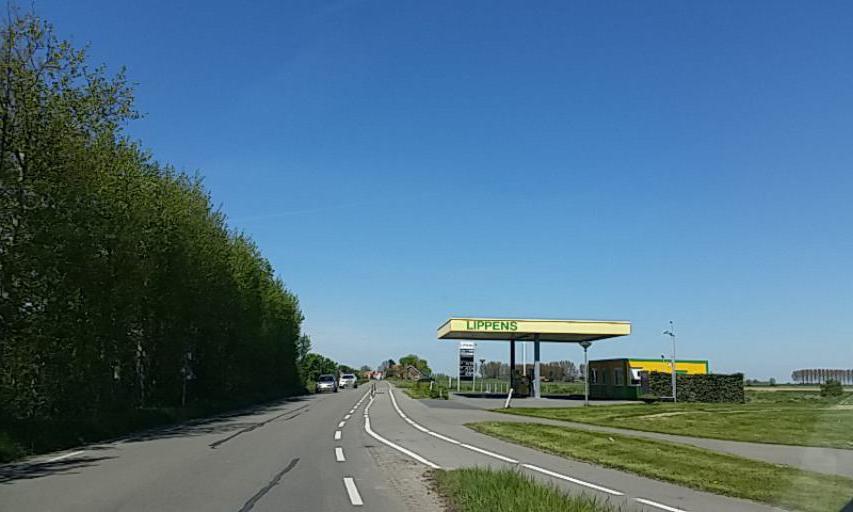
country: NL
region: Zeeland
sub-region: Gemeente Borsele
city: Borssele
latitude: 51.3380
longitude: 3.6620
